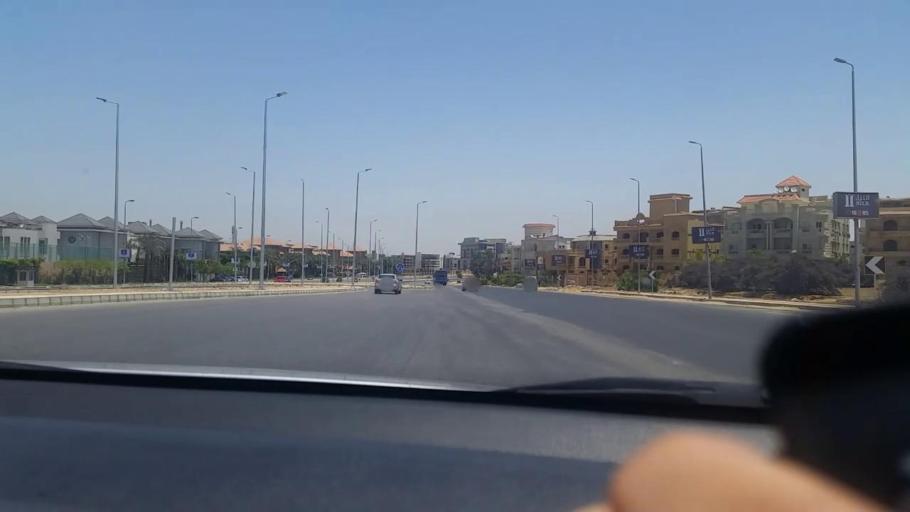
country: EG
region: Muhafazat al Qalyubiyah
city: Al Khankah
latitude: 30.0222
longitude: 31.4529
